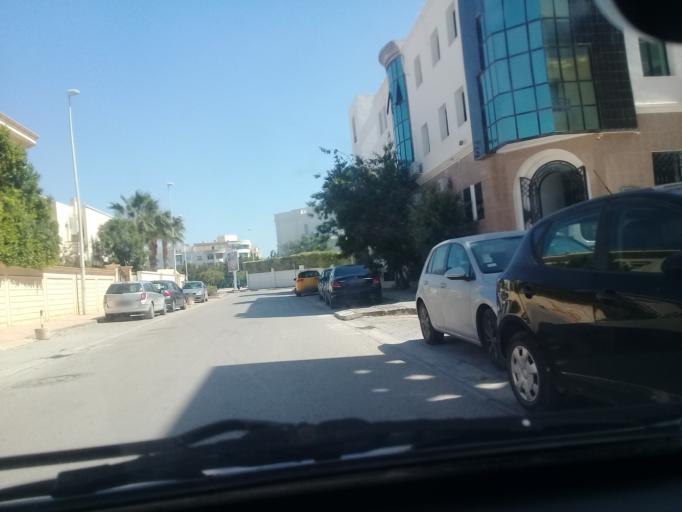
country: TN
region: Ariana
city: Ariana
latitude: 36.8396
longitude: 10.2459
